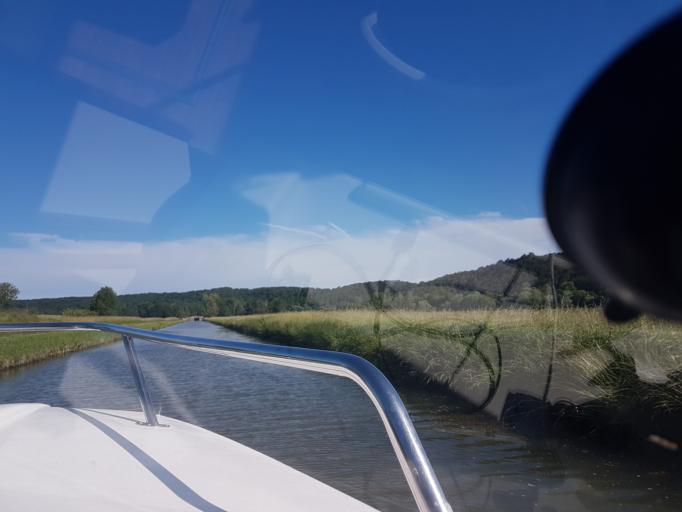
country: FR
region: Bourgogne
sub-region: Departement de la Nievre
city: Clamecy
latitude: 47.5345
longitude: 3.6124
